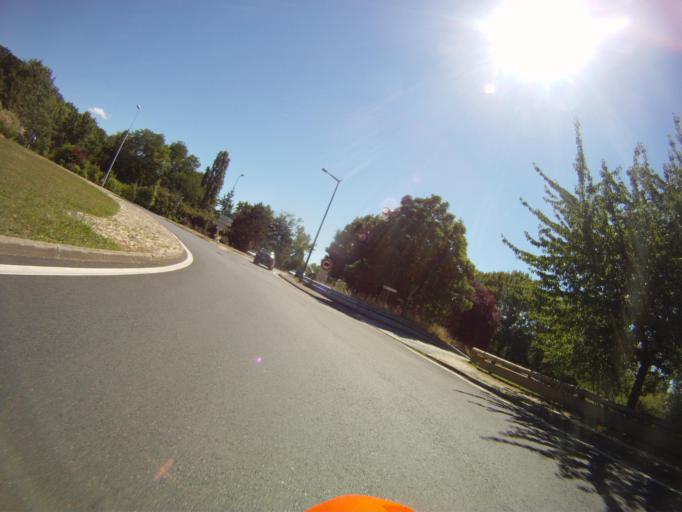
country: FR
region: Centre
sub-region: Departement d'Indre-et-Loire
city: Rochecorbon
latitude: 47.4178
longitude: 0.7508
